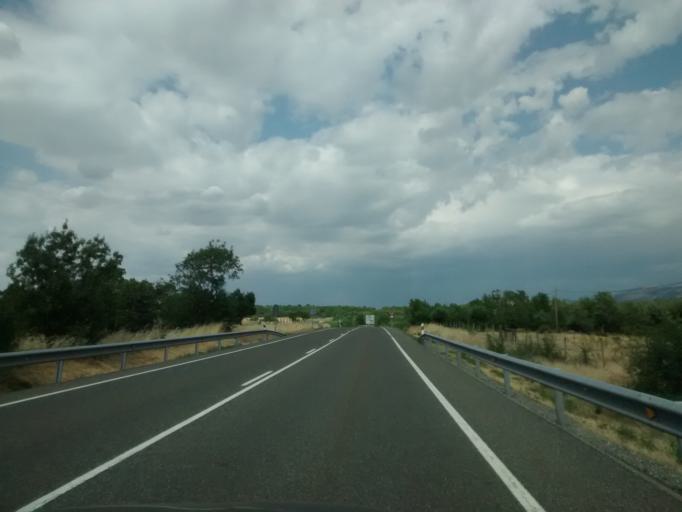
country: ES
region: Castille and Leon
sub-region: Provincia de Segovia
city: Gallegos
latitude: 41.0732
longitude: -3.8089
